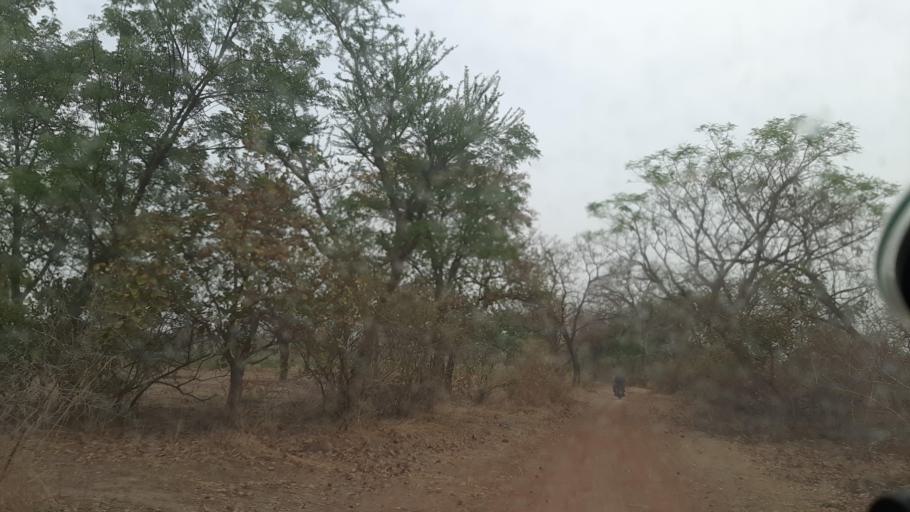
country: BF
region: Boucle du Mouhoun
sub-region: Province des Banwa
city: Salanso
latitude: 11.8494
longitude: -4.4229
